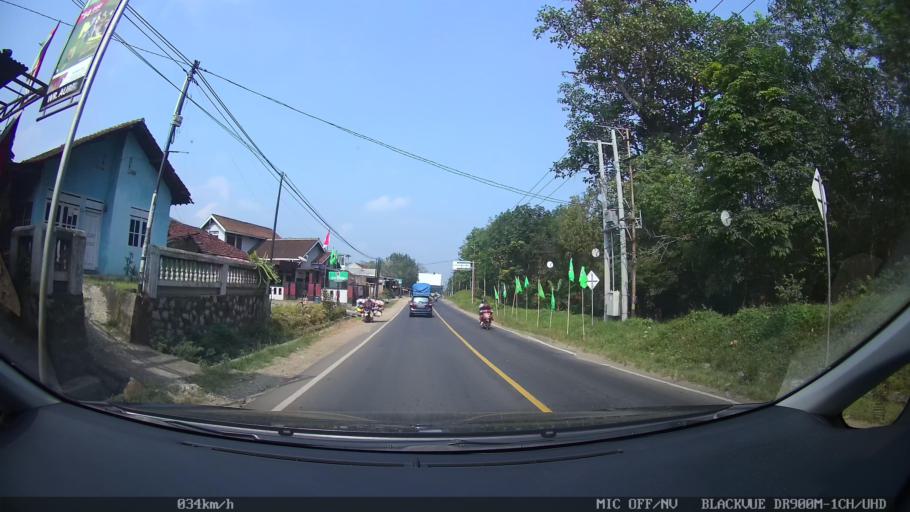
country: ID
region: Lampung
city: Gedongtataan
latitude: -5.3683
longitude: 105.1379
